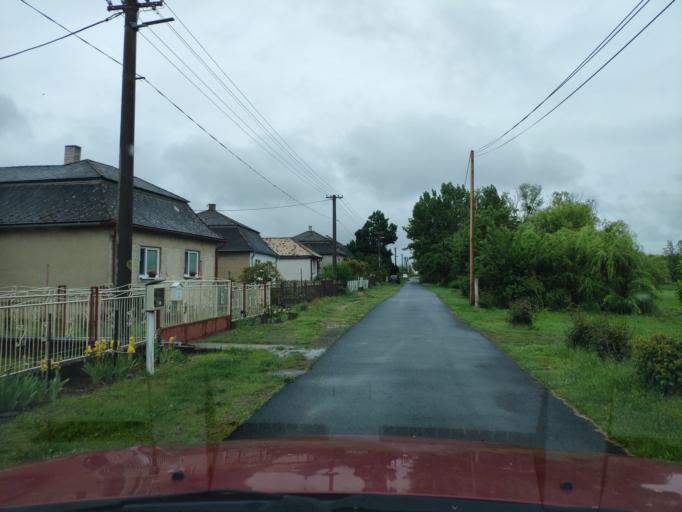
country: SK
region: Kosicky
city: Cierna nad Tisou
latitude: 48.4087
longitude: 22.0624
